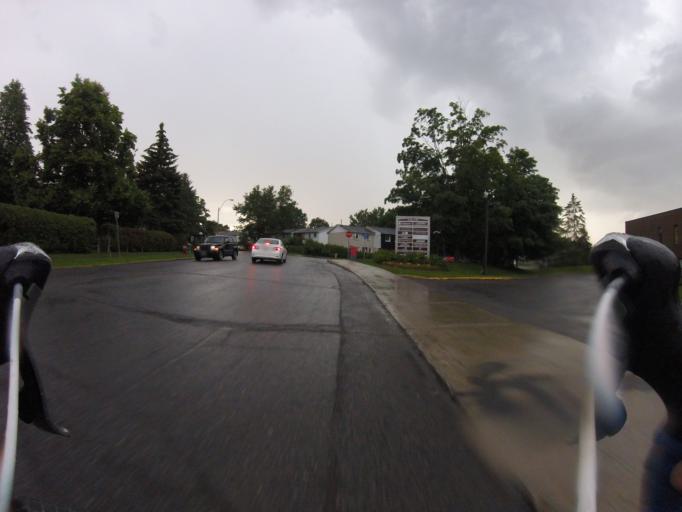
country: CA
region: Ontario
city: Bells Corners
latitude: 45.3448
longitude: -75.7971
